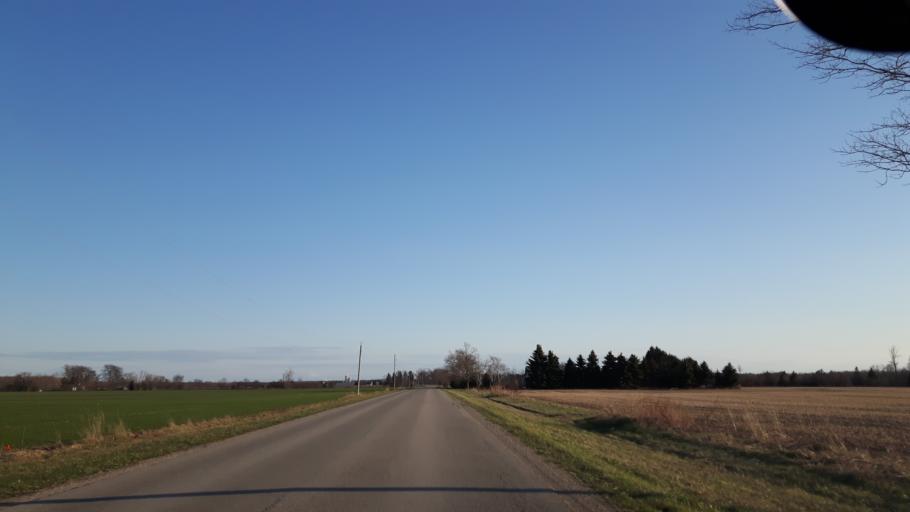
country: CA
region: Ontario
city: Goderich
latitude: 43.6496
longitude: -81.6846
